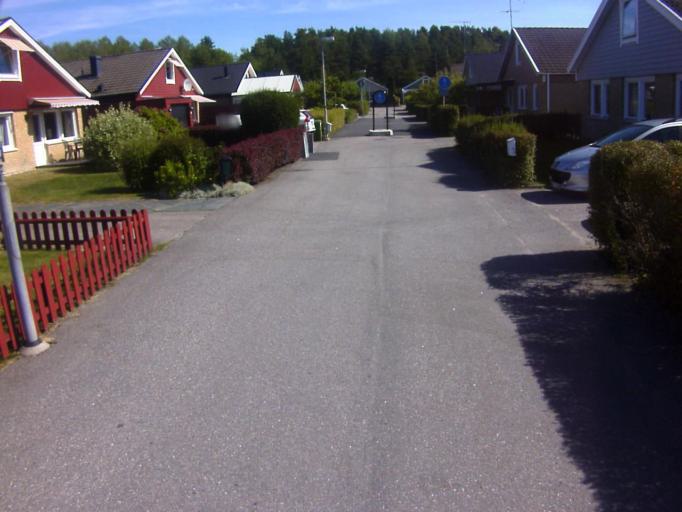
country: SE
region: Soedermanland
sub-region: Eskilstuna Kommun
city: Arla
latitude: 59.4018
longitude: 16.8202
